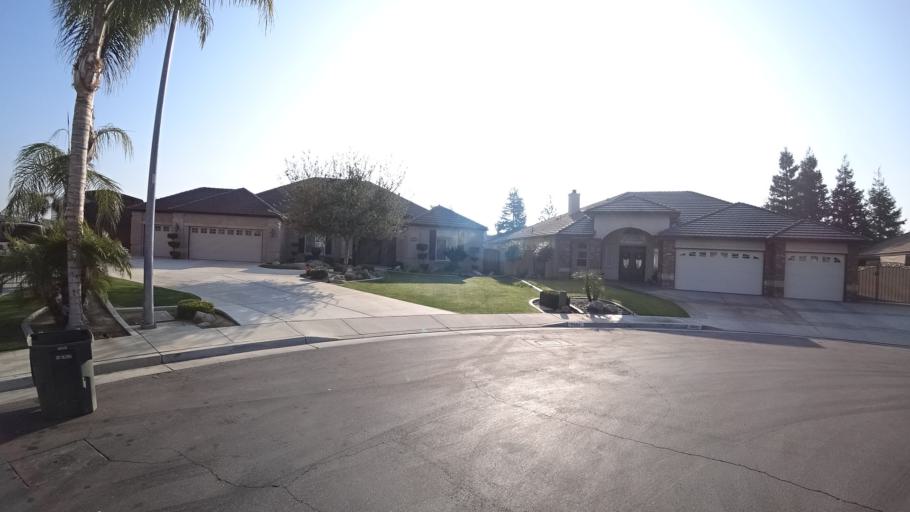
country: US
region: California
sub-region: Kern County
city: Greenacres
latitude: 35.3976
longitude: -119.1031
